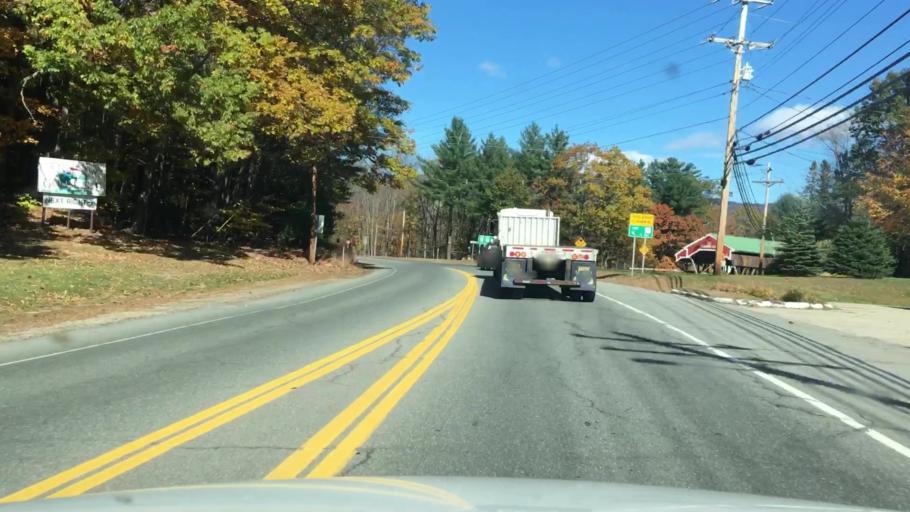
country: US
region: New Hampshire
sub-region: Carroll County
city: North Conway
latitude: 44.1406
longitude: -71.1873
